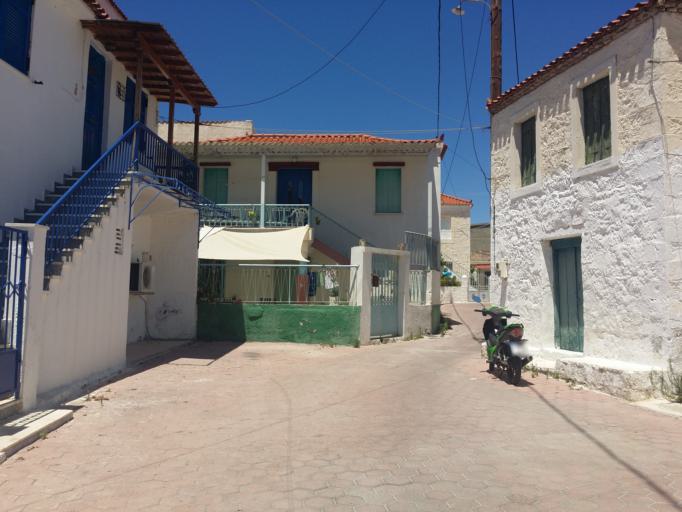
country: GR
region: Attica
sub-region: Nomos Piraios
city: Megalochori
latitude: 37.7108
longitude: 23.3459
